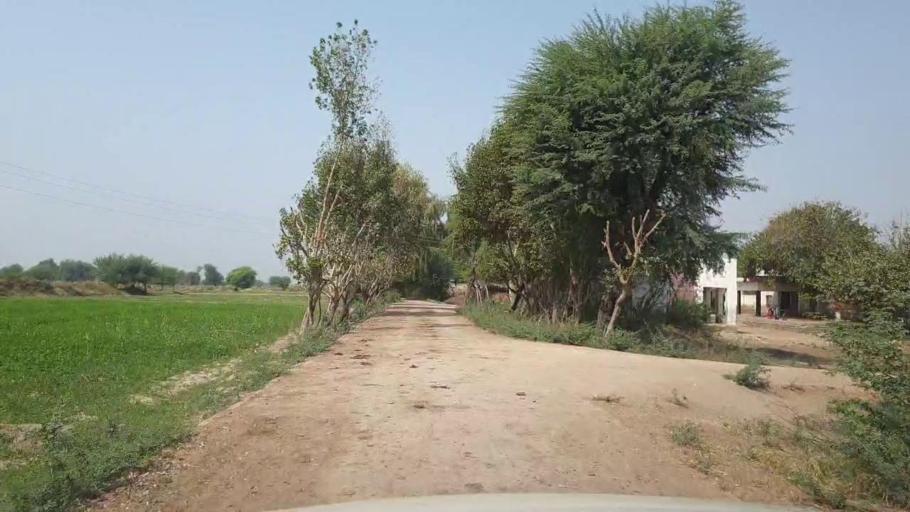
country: PK
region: Sindh
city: Chor
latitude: 25.4758
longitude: 69.6761
